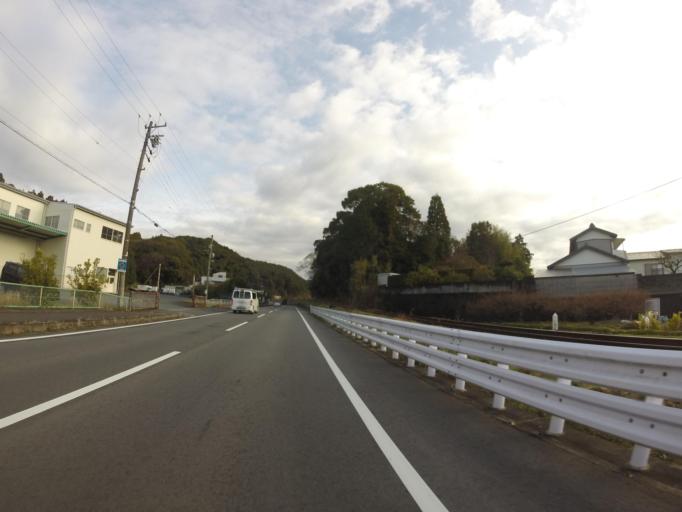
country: JP
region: Shizuoka
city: Hamakita
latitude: 34.8230
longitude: 137.7143
